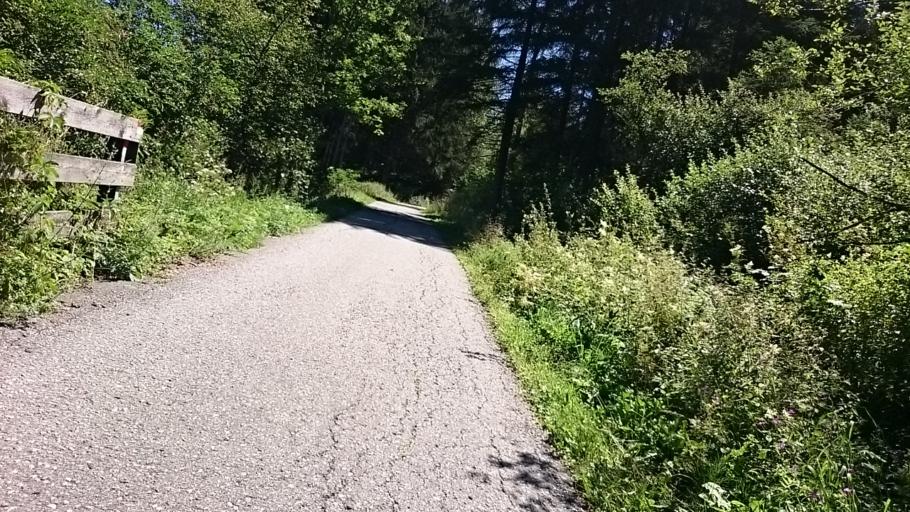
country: IT
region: Trentino-Alto Adige
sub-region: Bolzano
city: Chienes
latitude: 46.7953
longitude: 11.8490
